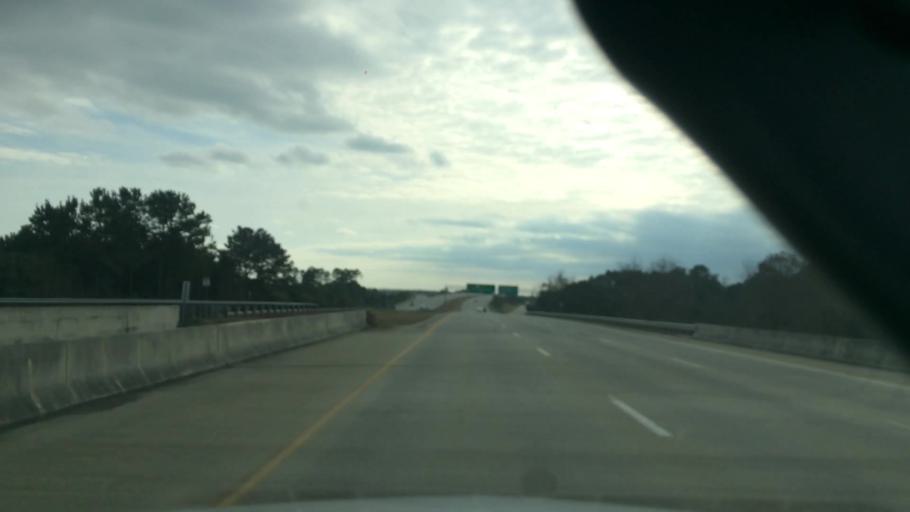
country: US
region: South Carolina
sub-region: Horry County
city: North Myrtle Beach
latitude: 33.8523
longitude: -78.6983
